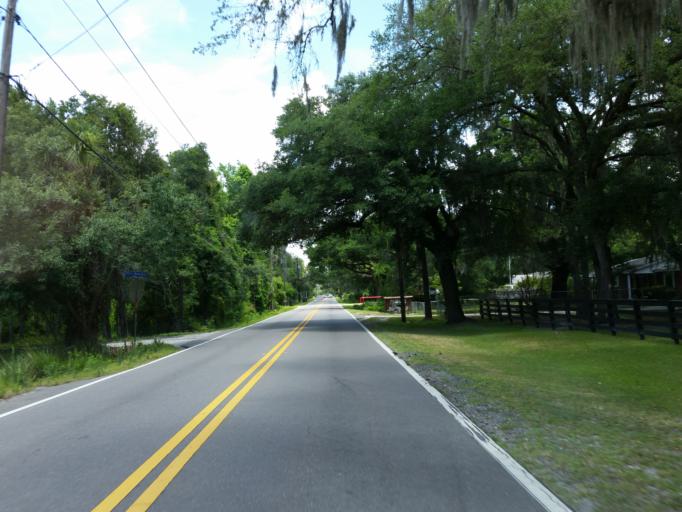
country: US
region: Florida
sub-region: Hillsborough County
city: Dover
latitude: 28.0016
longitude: -82.2445
